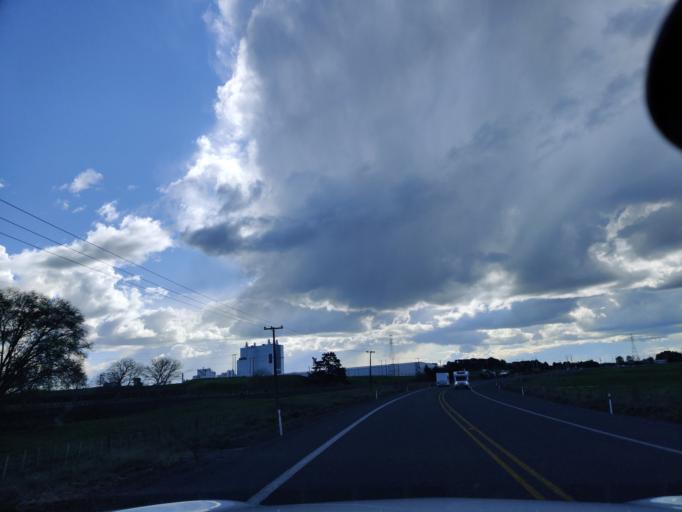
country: NZ
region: Waikato
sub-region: South Waikato District
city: Tokoroa
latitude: -38.1395
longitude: 175.8299
